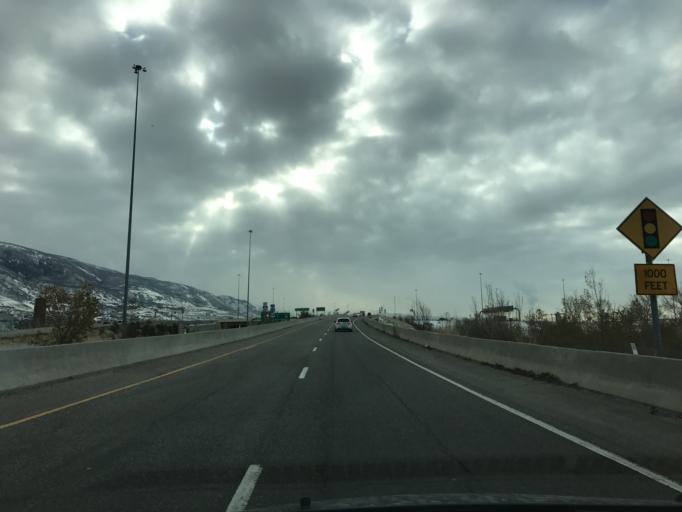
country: US
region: Utah
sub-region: Davis County
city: Farmington
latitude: 40.9939
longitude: -111.9046
